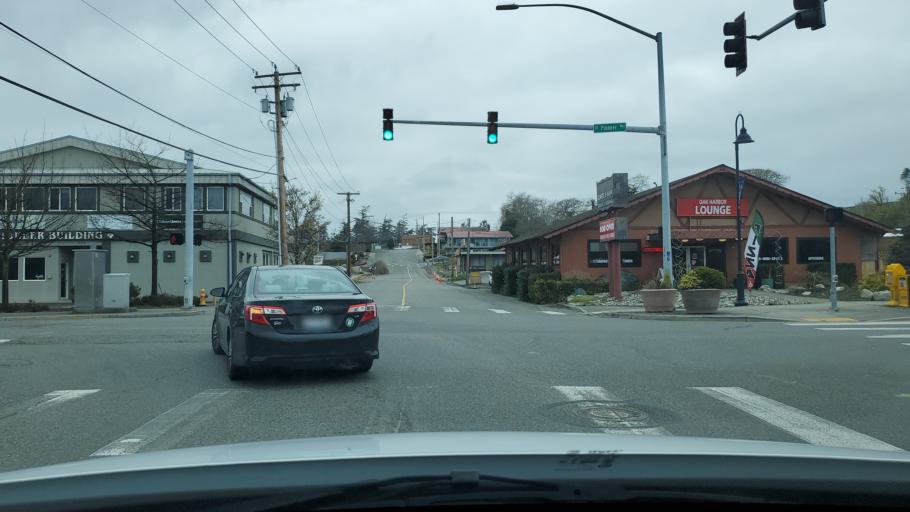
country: US
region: Washington
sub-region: Island County
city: Oak Harbor
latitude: 48.2879
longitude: -122.6526
